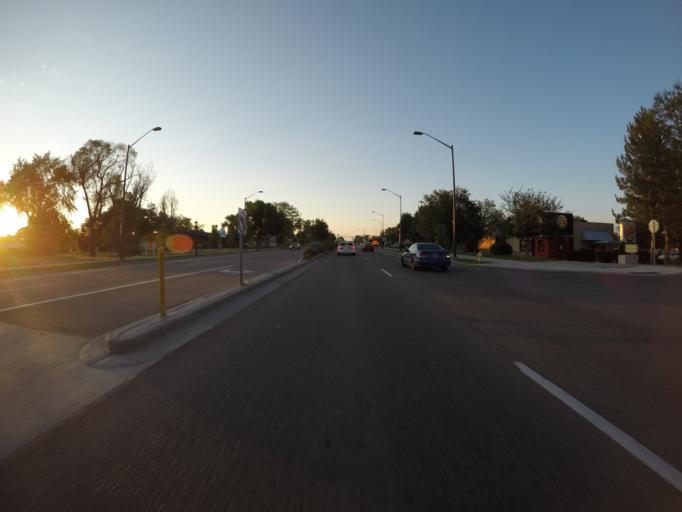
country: US
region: Colorado
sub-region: Larimer County
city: Fort Collins
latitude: 40.6088
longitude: -105.0765
